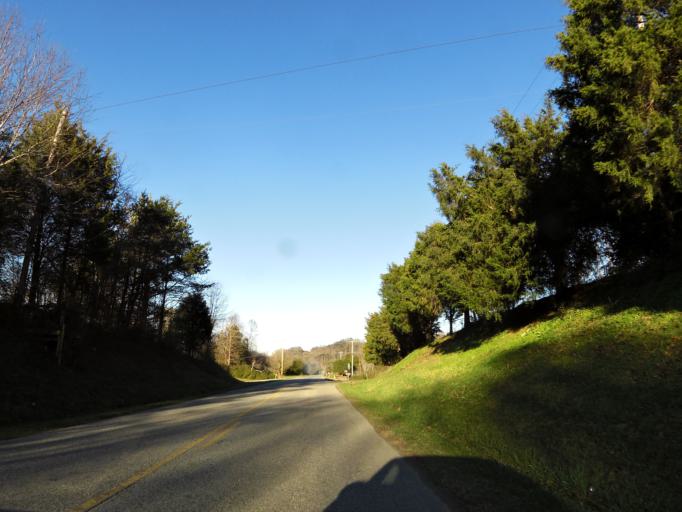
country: US
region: Tennessee
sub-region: Anderson County
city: Clinton
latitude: 36.1518
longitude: -84.1748
